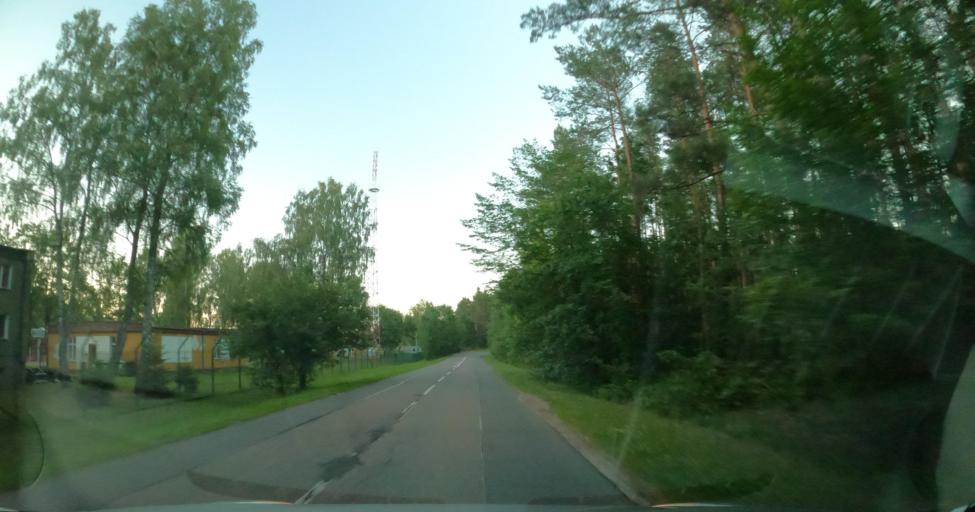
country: PL
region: Pomeranian Voivodeship
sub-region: Powiat wejherowski
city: Linia
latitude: 54.4666
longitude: 17.9874
